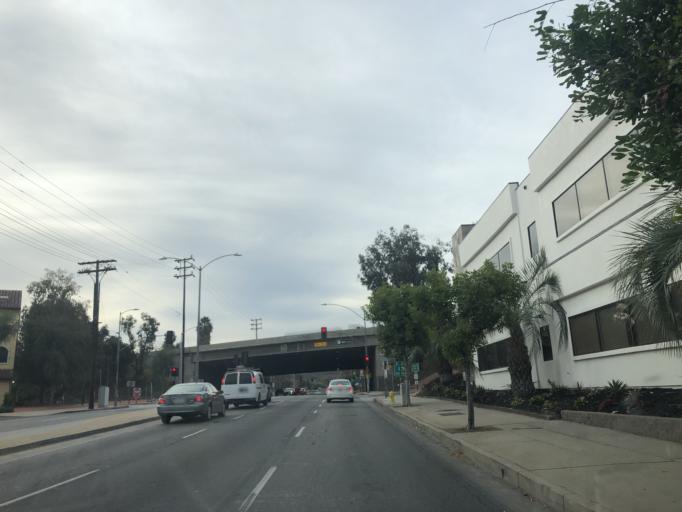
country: US
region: California
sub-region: Los Angeles County
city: Van Nuys
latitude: 34.1715
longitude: -118.5012
